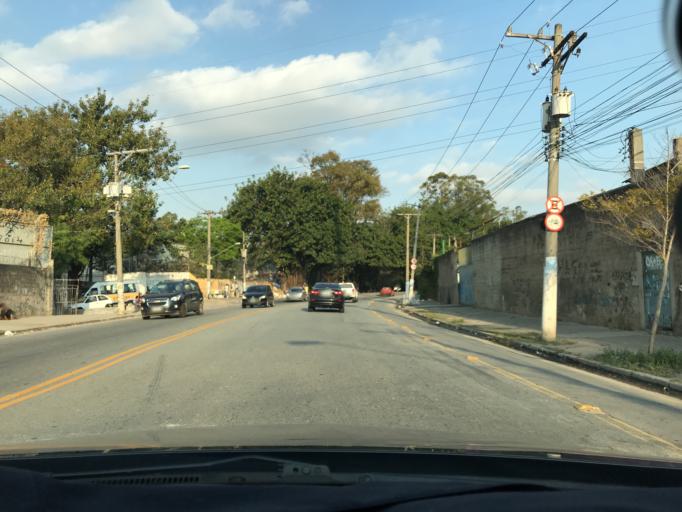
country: BR
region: Sao Paulo
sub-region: Osasco
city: Osasco
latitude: -23.5313
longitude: -46.7564
